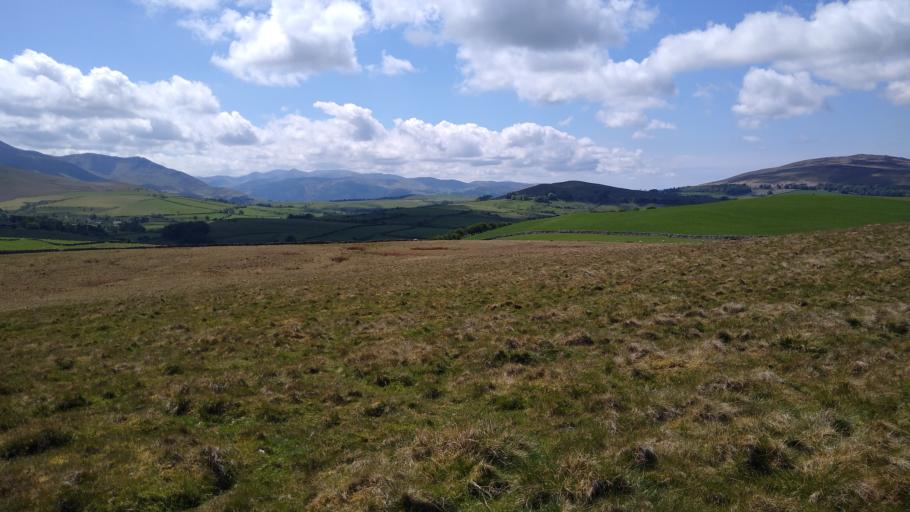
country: GB
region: England
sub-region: Cumbria
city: Wigton
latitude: 54.7246
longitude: -3.1449
